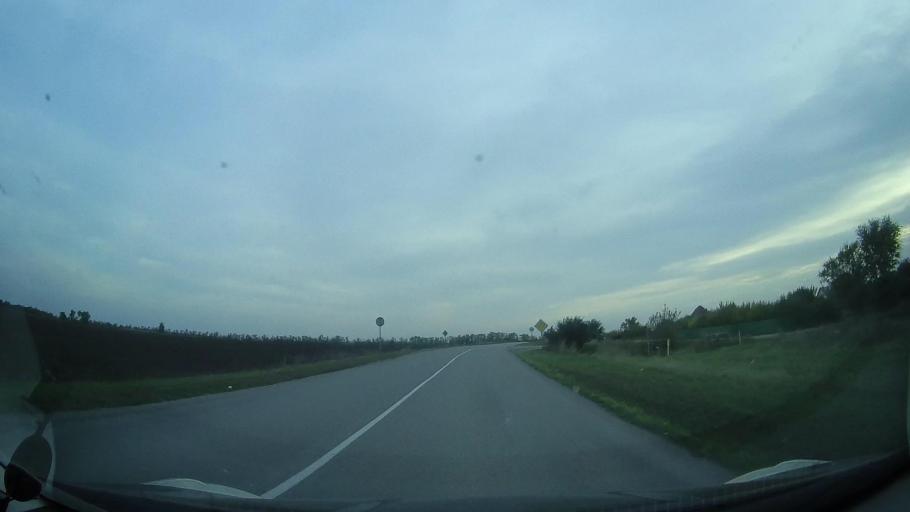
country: RU
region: Rostov
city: Kirovskaya
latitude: 47.0323
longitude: 39.9815
